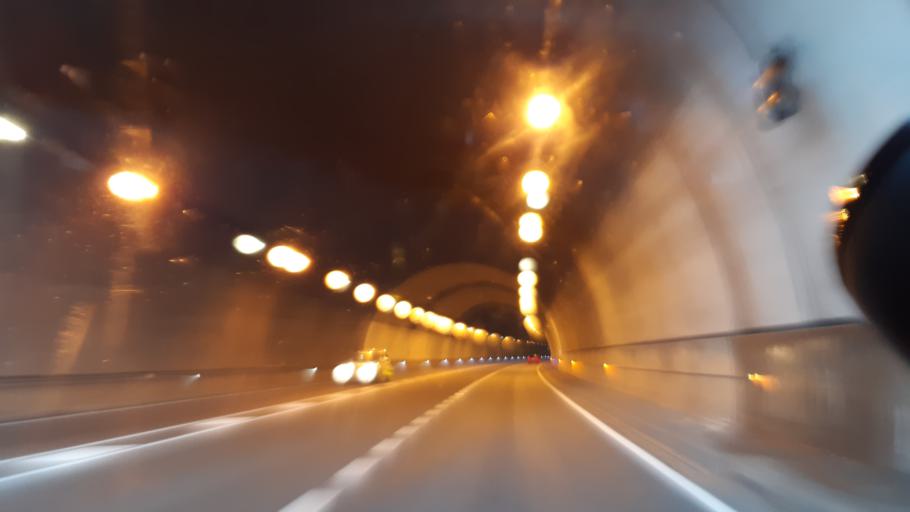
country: ES
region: Catalonia
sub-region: Provincia de Girona
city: Bas
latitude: 42.1249
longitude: 2.4290
